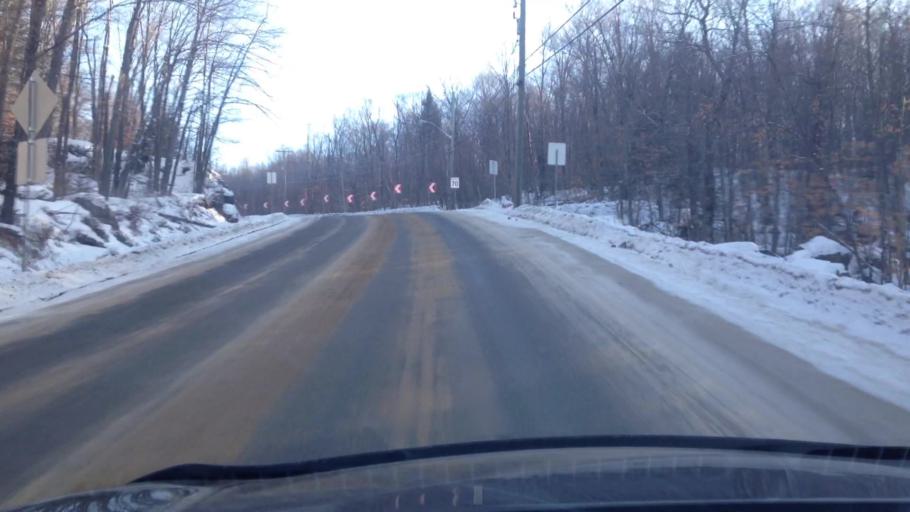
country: CA
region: Quebec
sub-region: Laurentides
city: Sainte-Agathe-des-Monts
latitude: 45.9316
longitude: -74.4602
